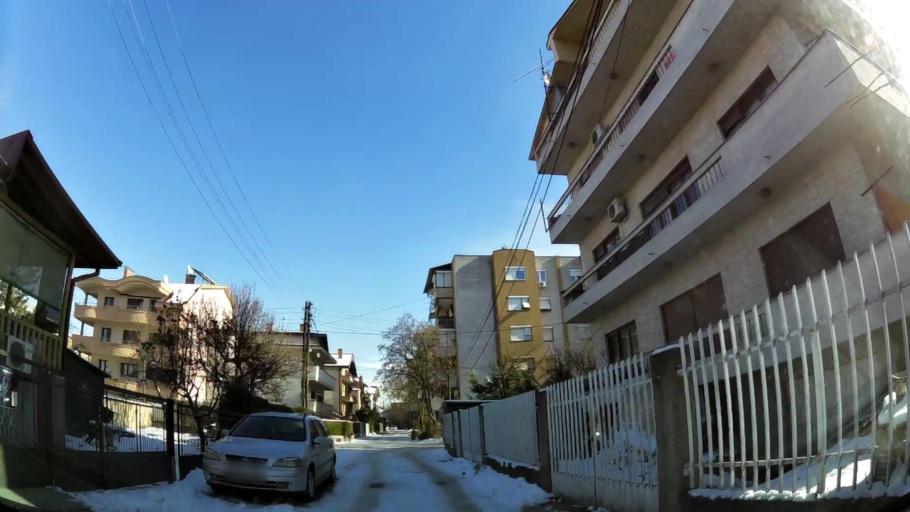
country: MK
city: Krushopek
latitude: 42.0053
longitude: 21.3565
